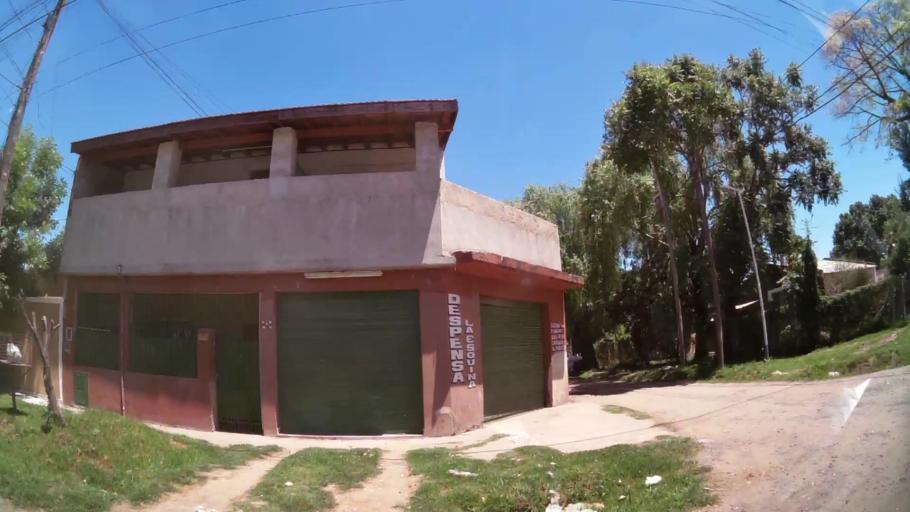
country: AR
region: Buenos Aires
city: Hurlingham
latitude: -34.5101
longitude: -58.7141
